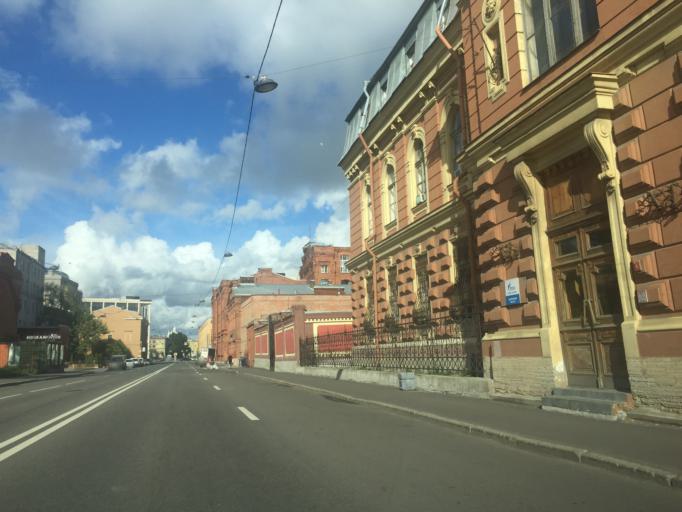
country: RU
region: St.-Petersburg
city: Centralniy
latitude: 59.9353
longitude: 30.3854
